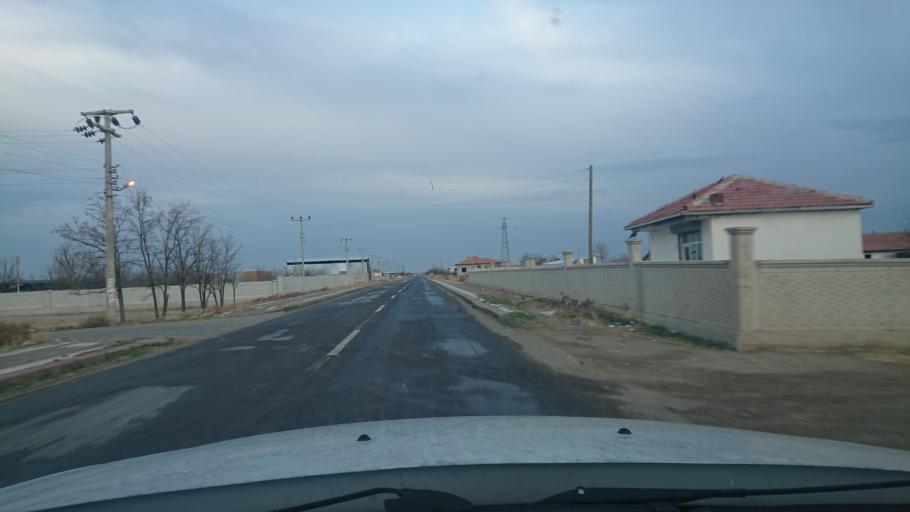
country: TR
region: Aksaray
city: Yesilova
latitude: 38.2948
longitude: 33.7591
